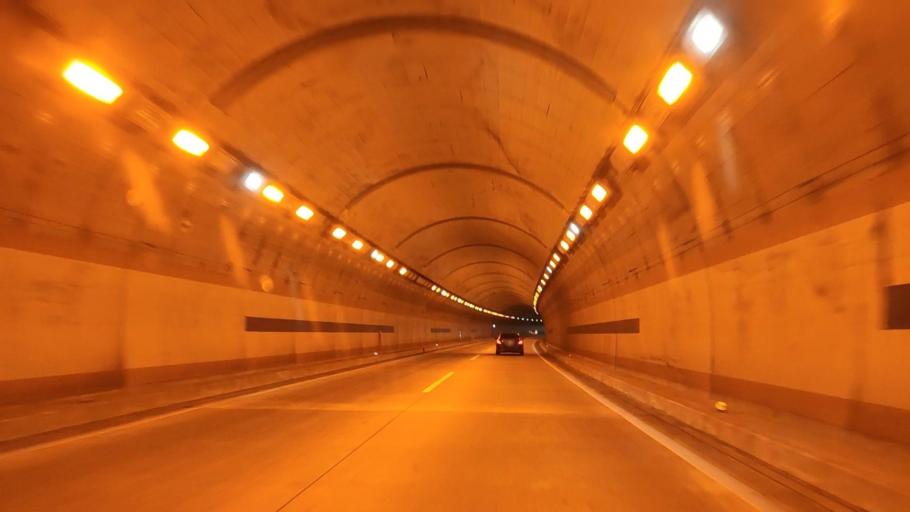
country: JP
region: Okayama
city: Kurashiki
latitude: 34.6169
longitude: 133.7400
